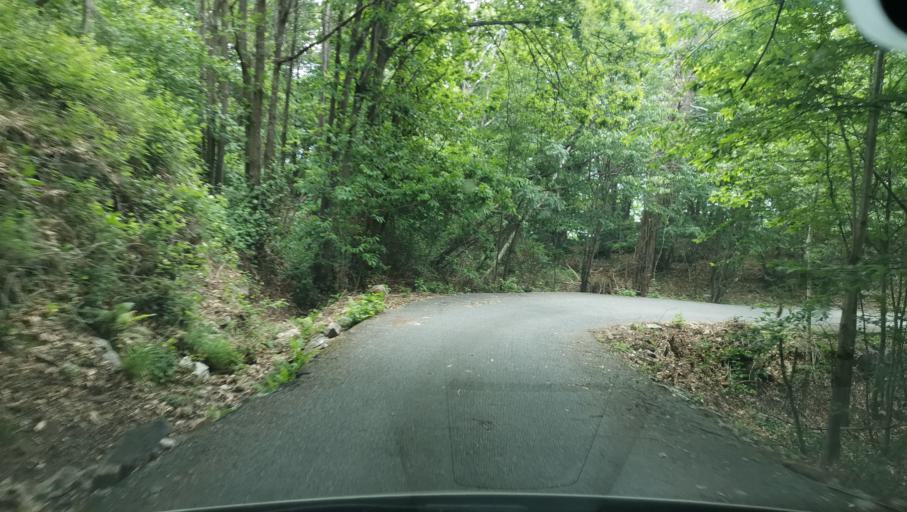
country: IT
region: Piedmont
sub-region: Provincia di Torino
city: Quassolo
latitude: 45.5316
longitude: 7.8273
